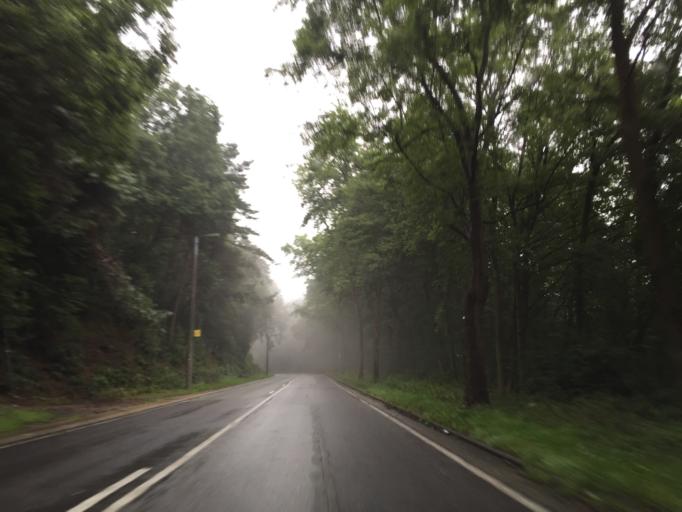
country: BE
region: Wallonia
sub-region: Province de Liege
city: Spa
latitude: 50.4997
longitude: 5.8836
